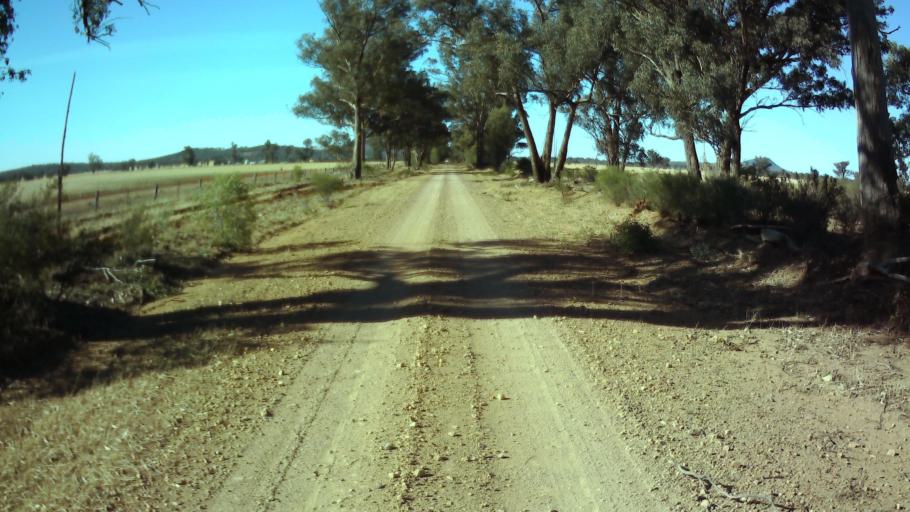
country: AU
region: New South Wales
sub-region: Weddin
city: Grenfell
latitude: -33.8245
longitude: 147.8746
